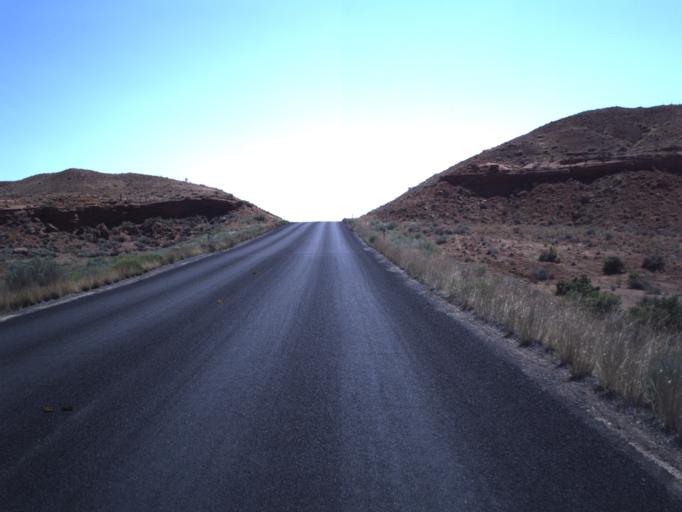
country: US
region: Utah
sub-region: Uintah County
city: Maeser
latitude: 40.4154
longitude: -109.7522
